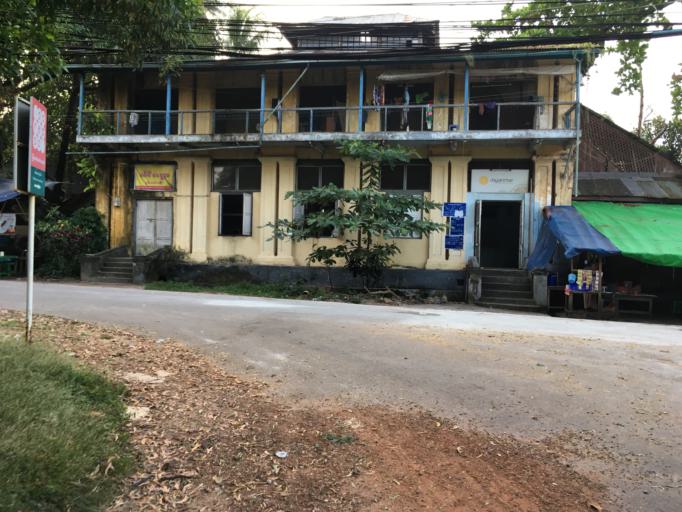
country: MM
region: Mon
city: Mawlamyine
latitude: 16.4829
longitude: 97.6203
